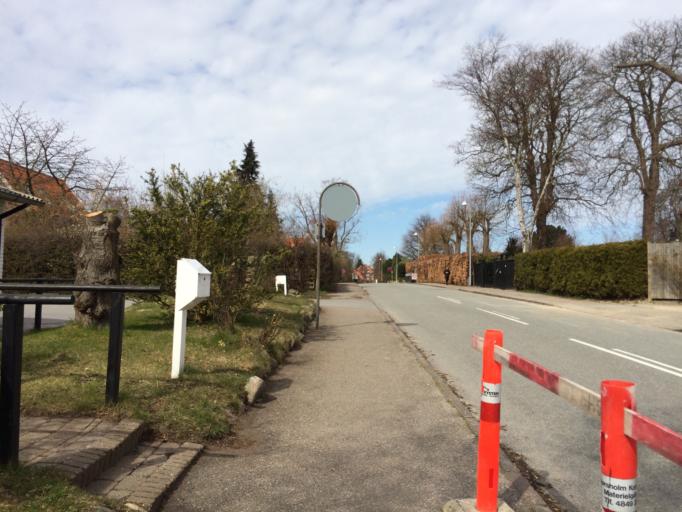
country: DK
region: Capital Region
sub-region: Horsholm Kommune
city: Horsholm
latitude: 55.8842
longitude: 12.5303
